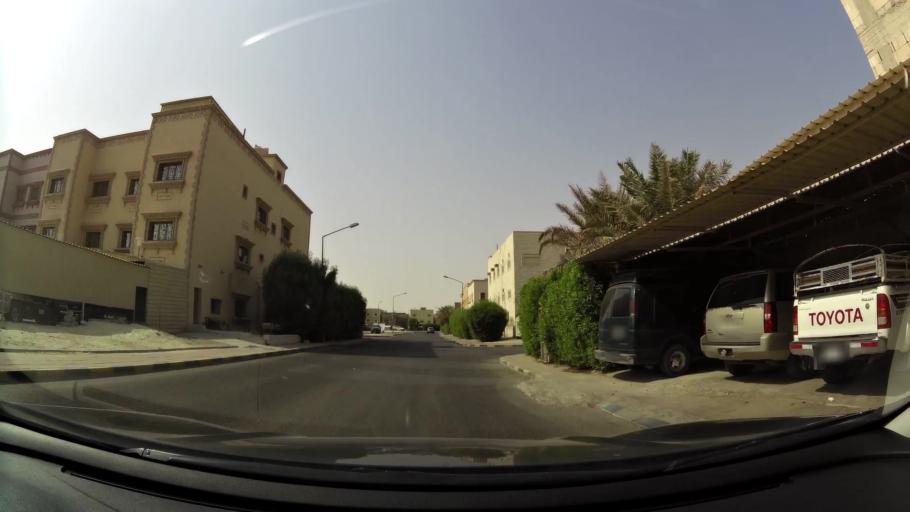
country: KW
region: Muhafazat al Jahra'
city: Al Jahra'
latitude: 29.3243
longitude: 47.6653
